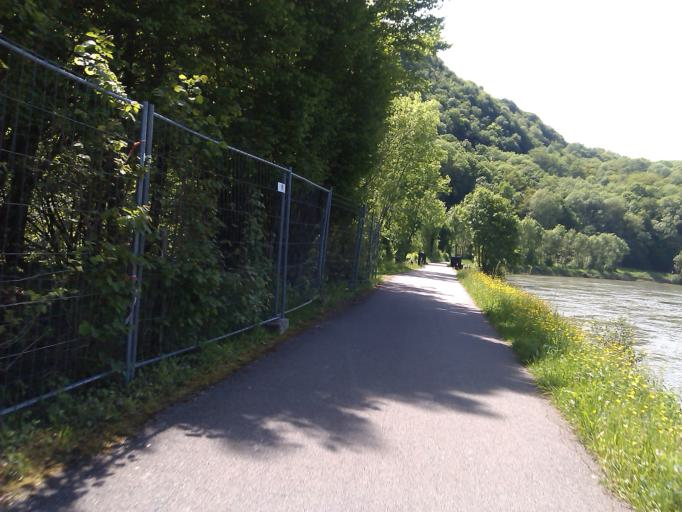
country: FR
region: Franche-Comte
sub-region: Departement du Doubs
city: Avanne-Aveney
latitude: 47.1987
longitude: 5.9865
